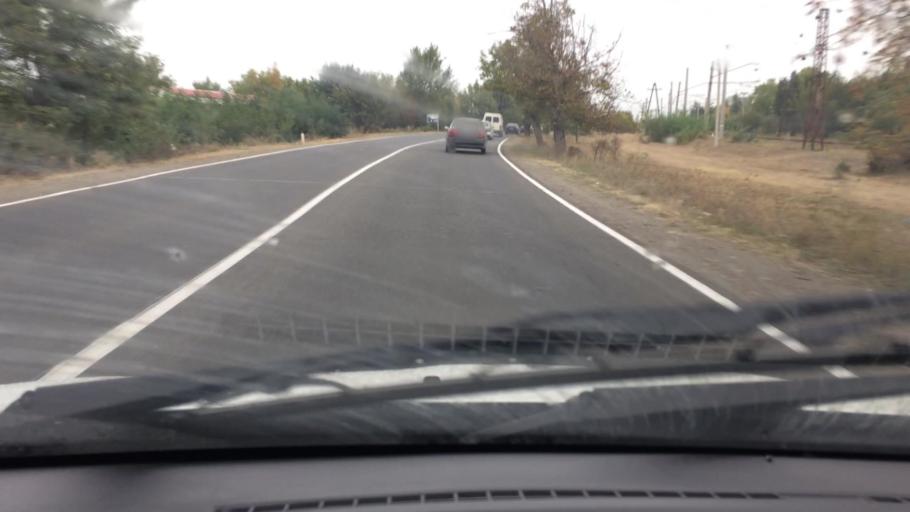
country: GE
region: Kvemo Kartli
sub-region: Marneuli
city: Marneuli
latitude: 41.4153
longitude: 44.8271
